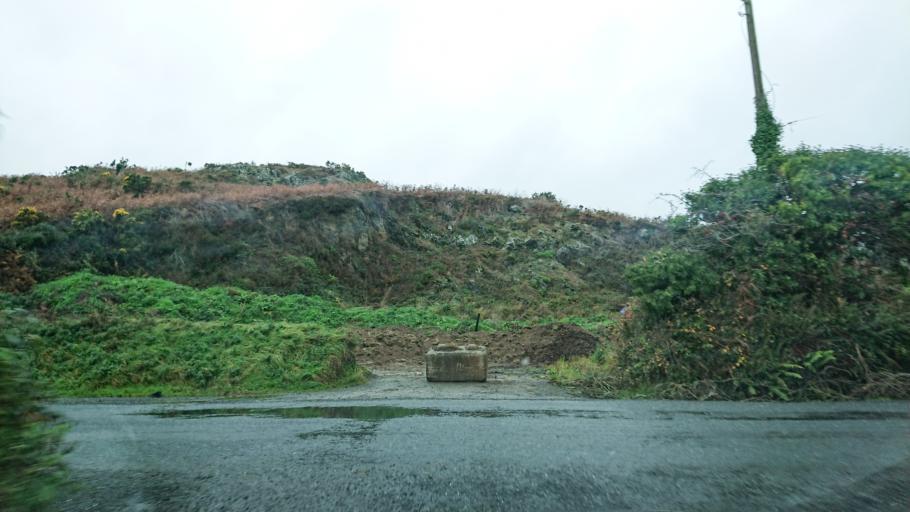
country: IE
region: Munster
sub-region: Waterford
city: Tra Mhor
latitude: 52.2030
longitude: -7.1785
